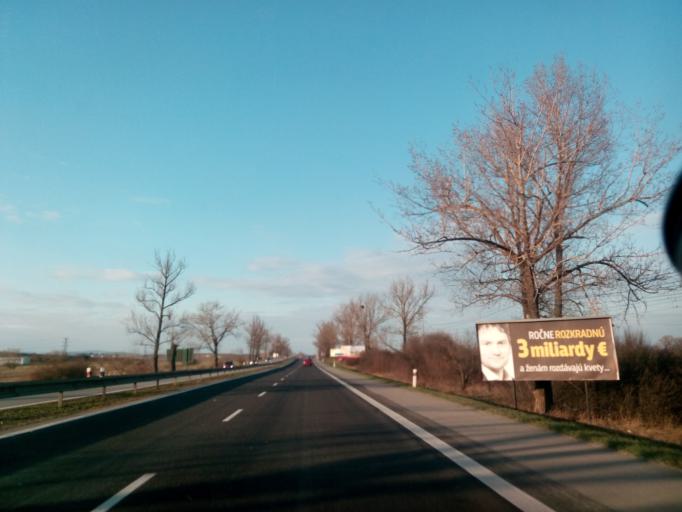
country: SK
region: Kosicky
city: Kosice
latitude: 48.6578
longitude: 21.2064
